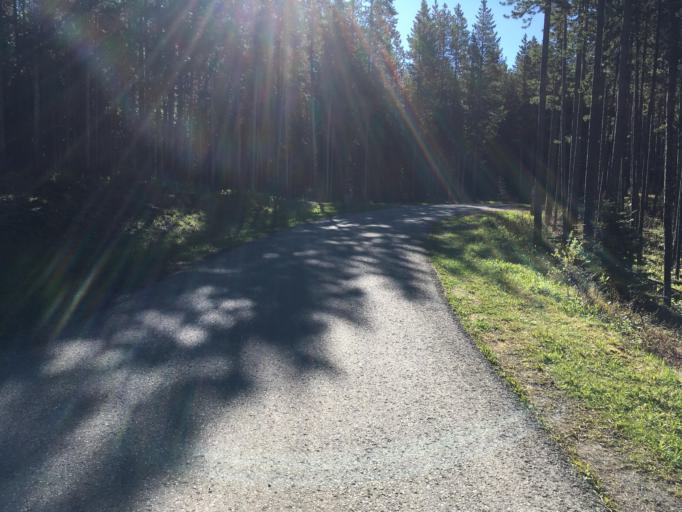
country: CA
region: Alberta
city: Canmore
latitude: 50.6356
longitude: -115.1003
